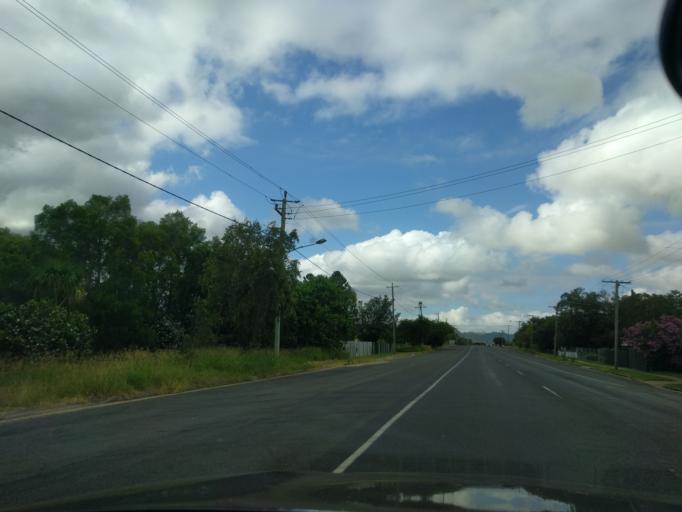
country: AU
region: Queensland
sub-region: Logan
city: Cedar Vale
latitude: -27.9927
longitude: 152.9919
